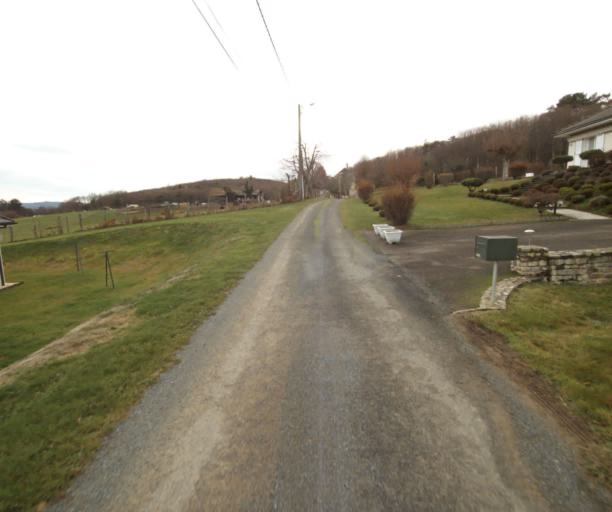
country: FR
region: Limousin
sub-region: Departement de la Correze
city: Chameyrat
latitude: 45.2669
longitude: 1.7010
